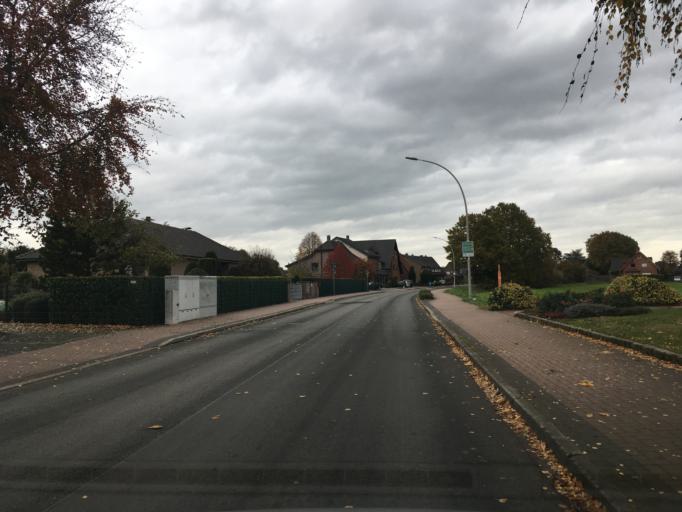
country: DE
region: North Rhine-Westphalia
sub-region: Regierungsbezirk Munster
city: Klein Reken
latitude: 51.8402
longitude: 7.0951
